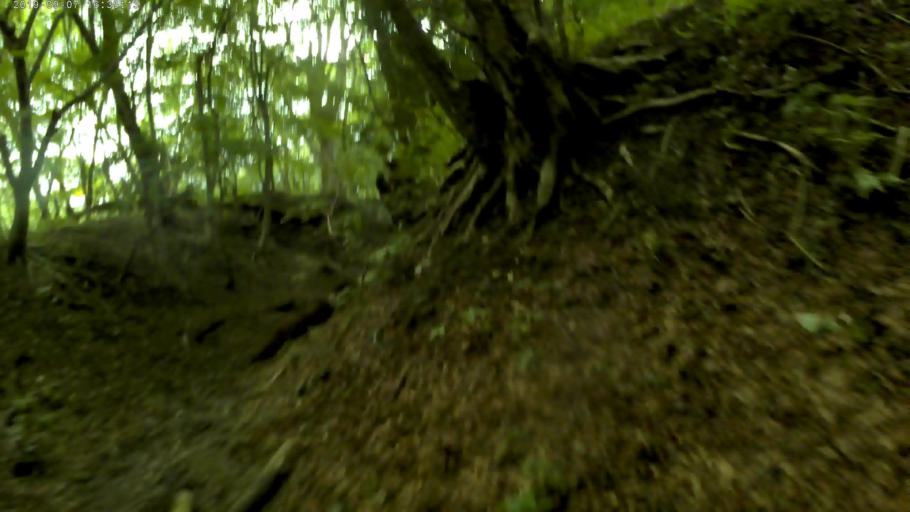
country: JP
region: Gunma
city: Annaka
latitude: 36.3640
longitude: 138.6933
